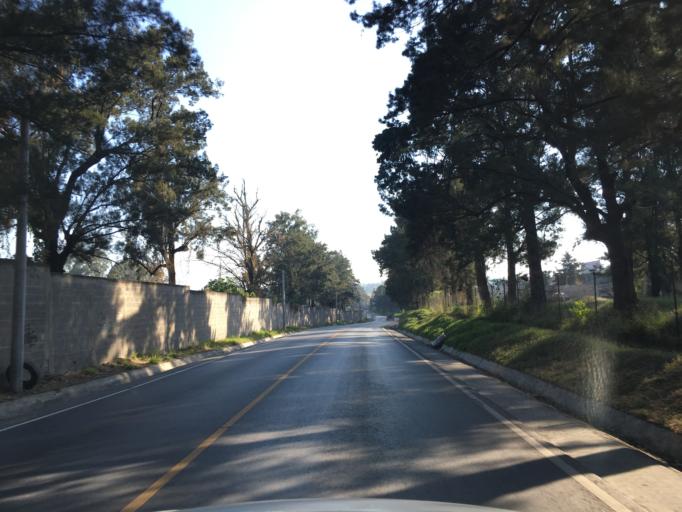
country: GT
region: Guatemala
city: Villa Nueva
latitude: 14.5304
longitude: -90.6167
